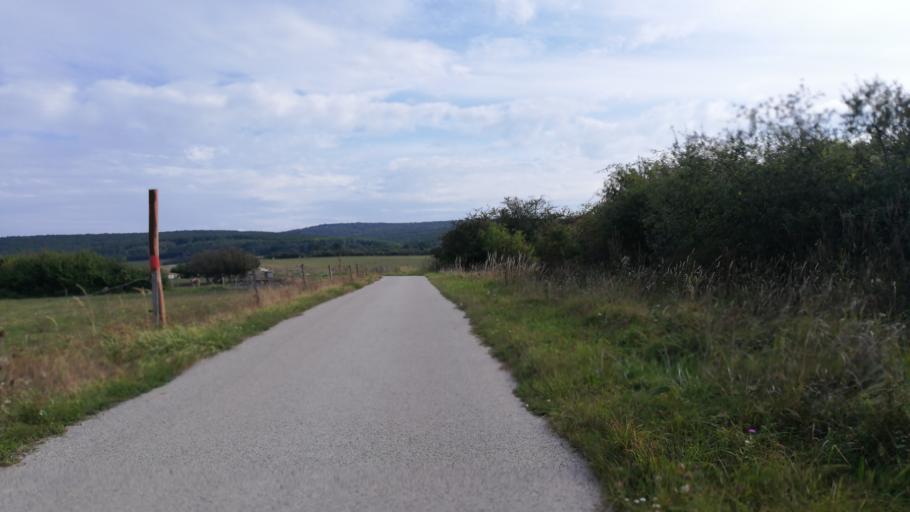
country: CZ
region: South Moravian
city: Petrov
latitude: 48.8379
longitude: 17.2928
